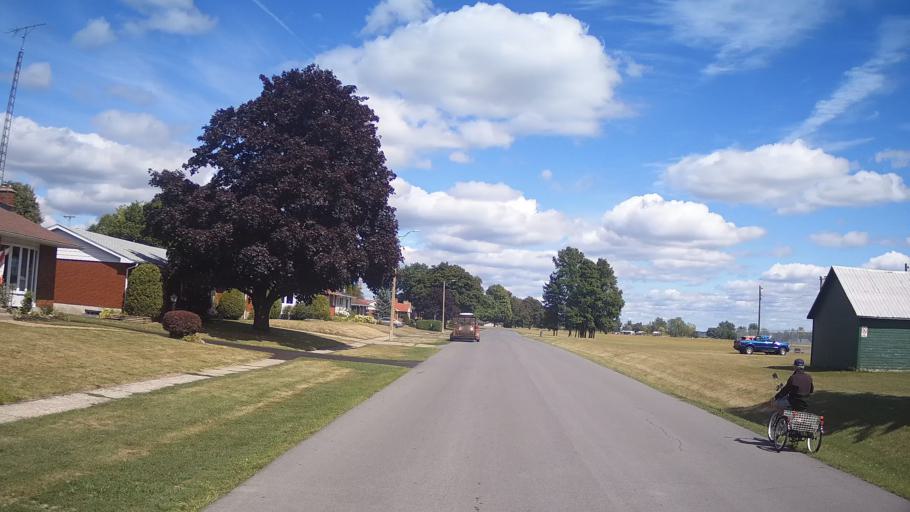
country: US
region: New York
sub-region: St. Lawrence County
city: Ogdensburg
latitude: 44.8414
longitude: -75.3179
